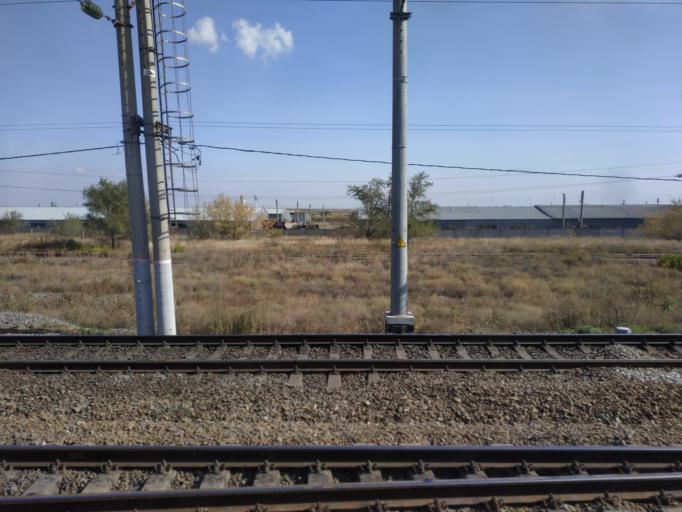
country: RU
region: Volgograd
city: Gumrak
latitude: 48.7892
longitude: 44.3689
